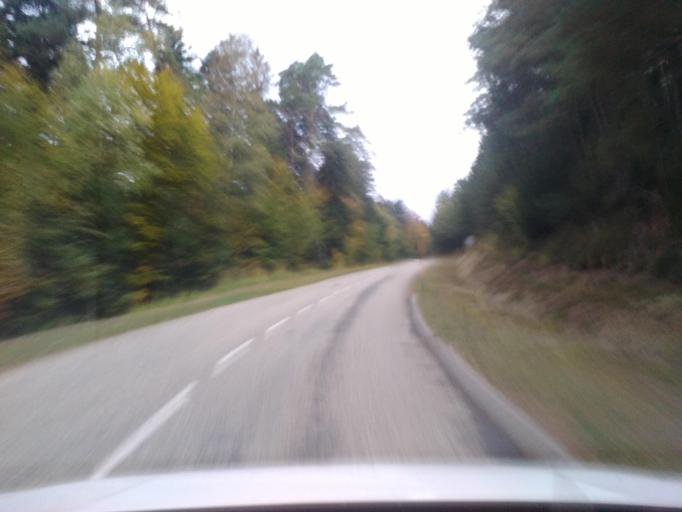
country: FR
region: Lorraine
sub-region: Departement des Vosges
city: Ban-de-Laveline
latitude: 48.3665
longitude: 7.1073
